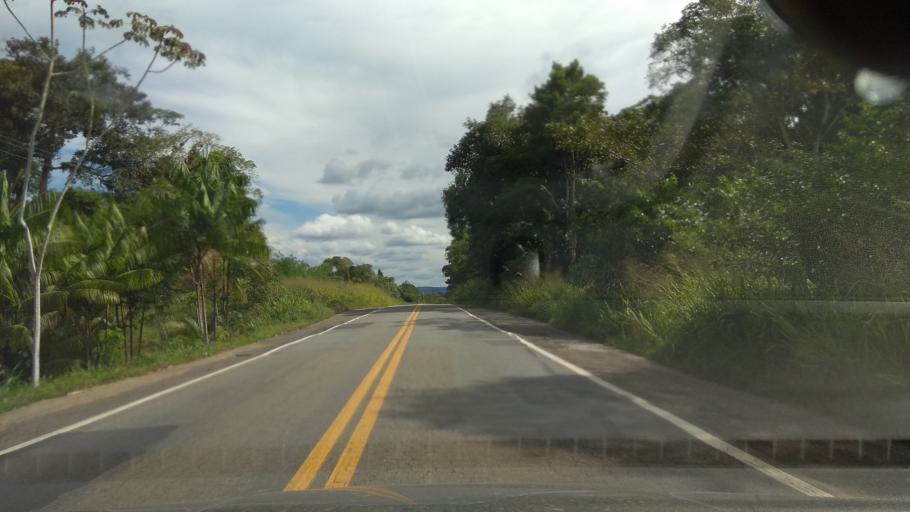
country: BR
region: Bahia
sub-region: Ubata
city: Ubata
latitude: -14.2296
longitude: -39.4503
